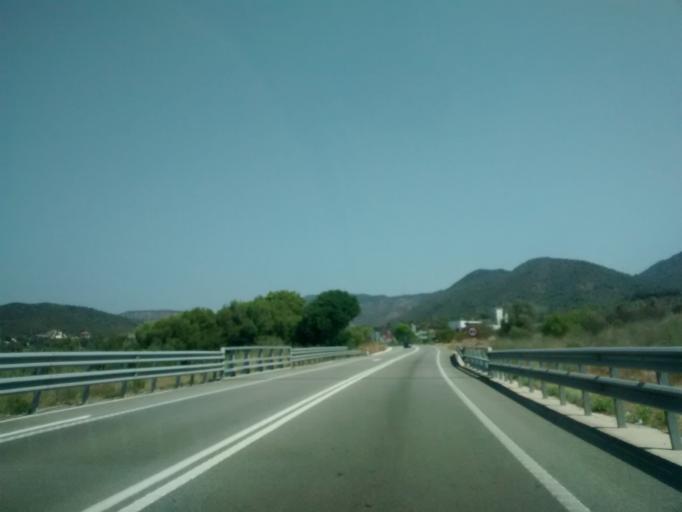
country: ES
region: Catalonia
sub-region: Provincia de Barcelona
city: Olesa de Montserrat
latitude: 41.5473
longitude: 1.8809
